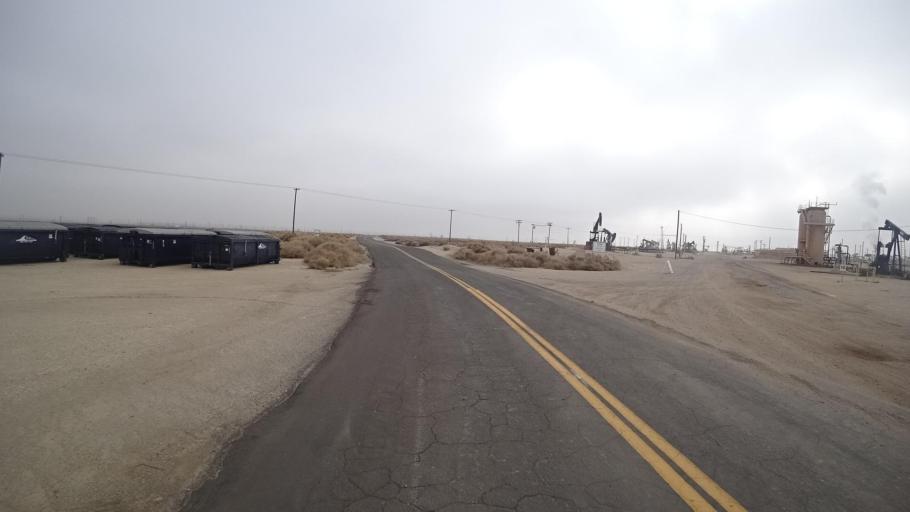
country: US
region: California
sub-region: Kern County
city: Maricopa
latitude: 35.0819
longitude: -119.3847
